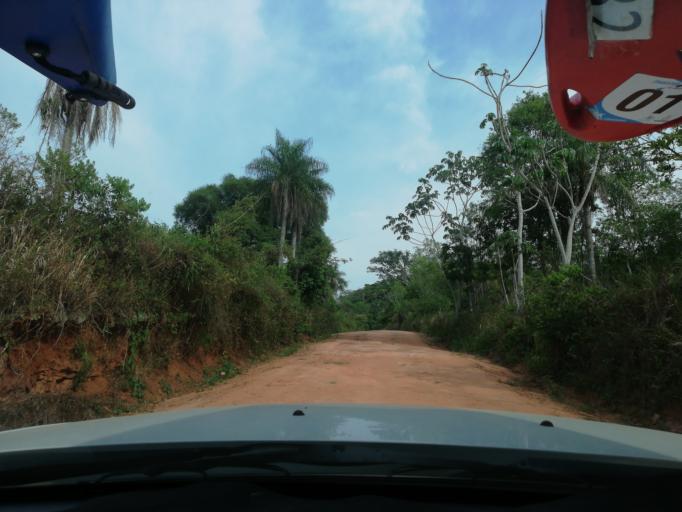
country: AR
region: Misiones
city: Santa Ana
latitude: -27.3061
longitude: -55.5833
